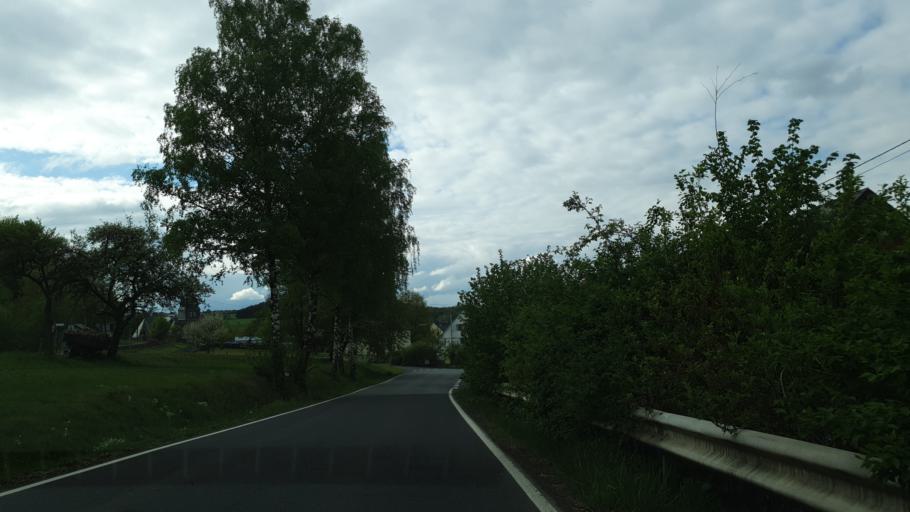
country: DE
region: Rheinland-Pfalz
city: Enspel
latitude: 50.6244
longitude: 7.8970
